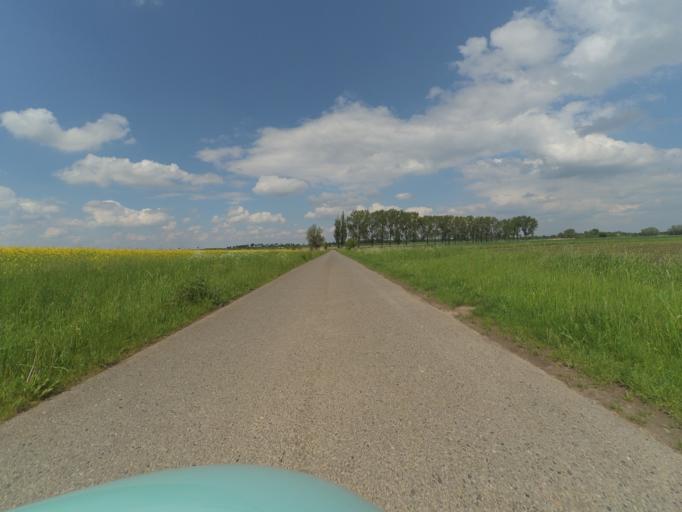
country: DE
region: Lower Saxony
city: Sehnde
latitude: 52.3044
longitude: 9.9165
